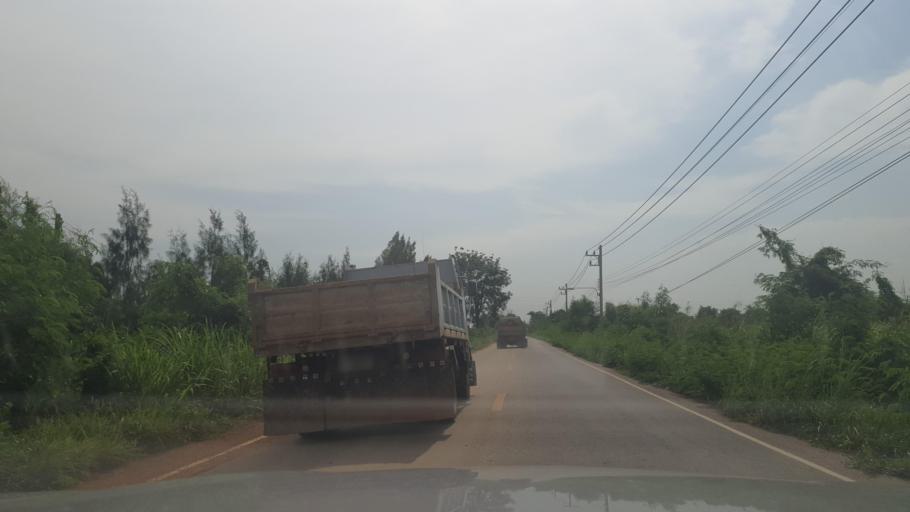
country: TH
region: Sukhothai
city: Si Samrong
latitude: 17.1179
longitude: 99.8730
